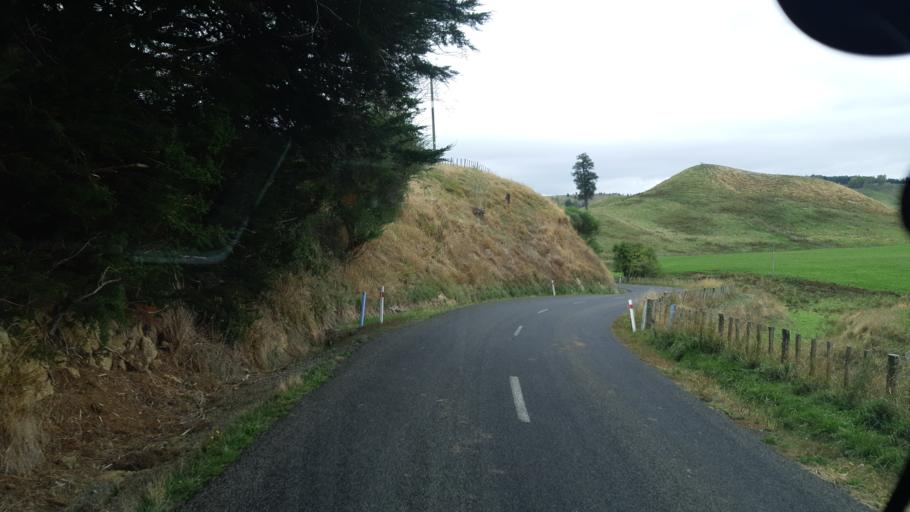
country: NZ
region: Manawatu-Wanganui
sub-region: Ruapehu District
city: Waiouru
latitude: -39.5551
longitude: 175.5883
